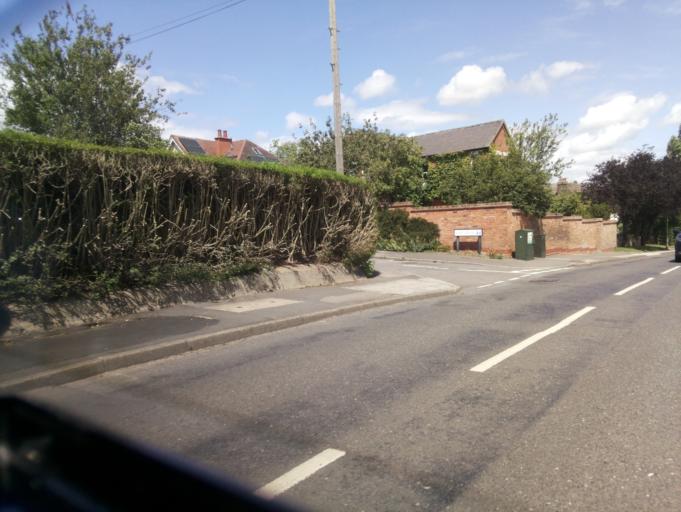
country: GB
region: England
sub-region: Nottinghamshire
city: Cotgrave
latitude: 52.8790
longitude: -1.0841
